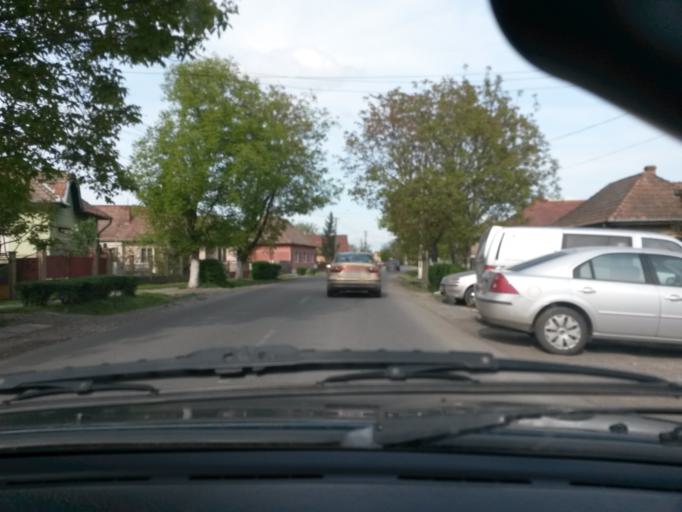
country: RO
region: Mures
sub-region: Comuna Sancraiu de Mures
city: Sancraiu de Mures
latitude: 46.5491
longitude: 24.5221
